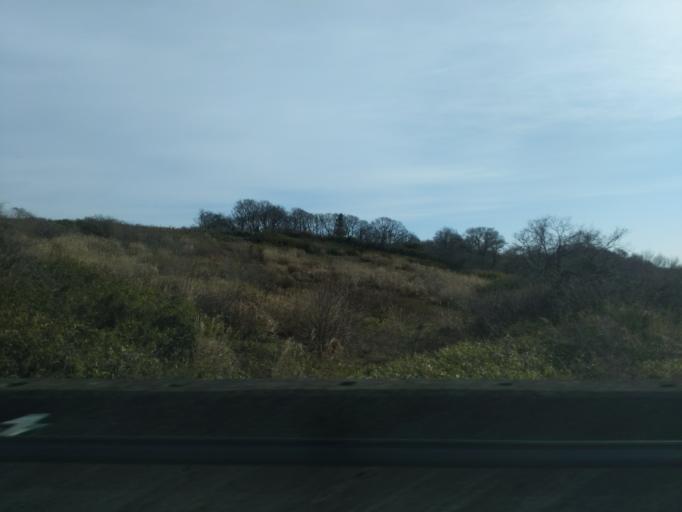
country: JP
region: Miyagi
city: Furukawa
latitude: 38.6629
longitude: 141.0230
